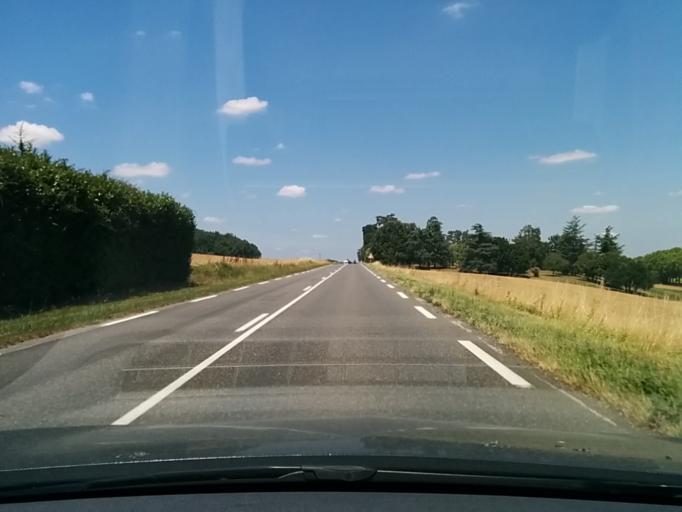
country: FR
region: Midi-Pyrenees
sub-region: Departement du Gers
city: Vic-Fezensac
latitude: 43.7294
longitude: 0.3753
